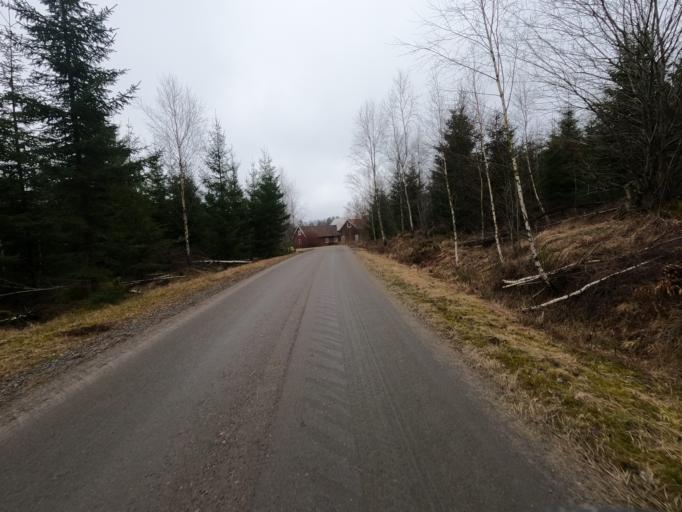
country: SE
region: Kronoberg
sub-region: Markaryds Kommun
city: Stromsnasbruk
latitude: 56.7988
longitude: 13.5589
